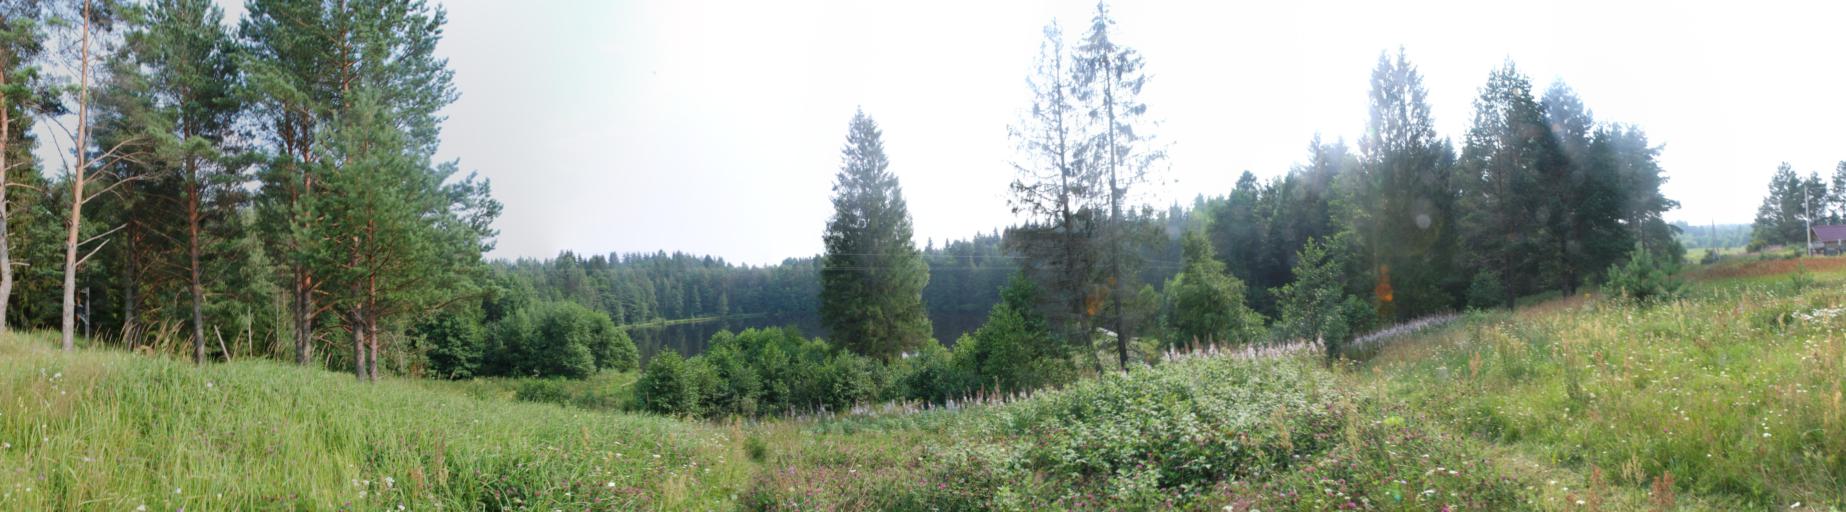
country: RU
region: Pskov
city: Strugi-Krasnyye
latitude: 57.8736
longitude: 29.0841
